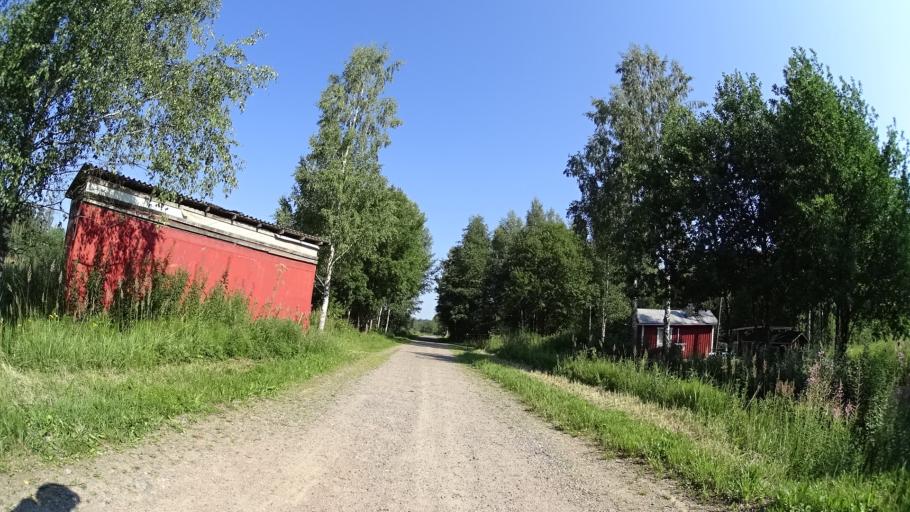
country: FI
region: Uusimaa
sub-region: Helsinki
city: Kerava
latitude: 60.3564
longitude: 25.1255
